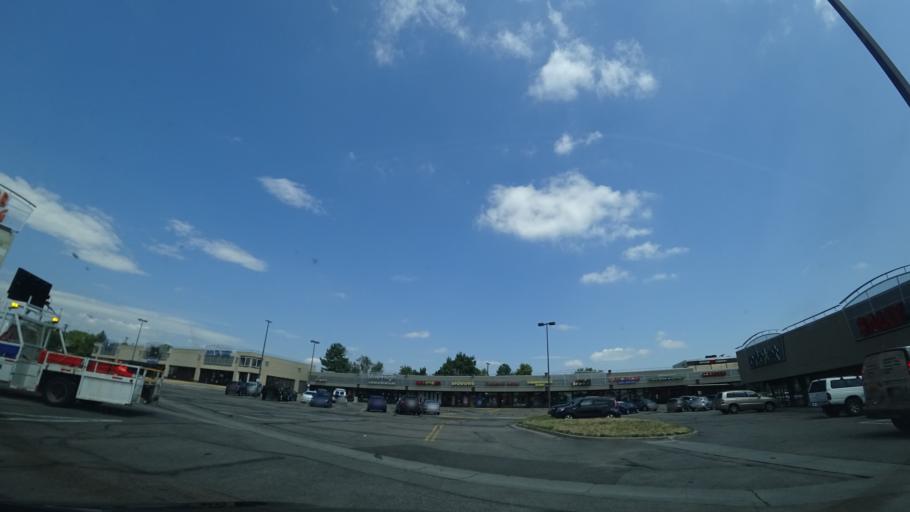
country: US
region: Colorado
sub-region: Jefferson County
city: Lakewood
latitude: 39.7113
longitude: -105.0751
